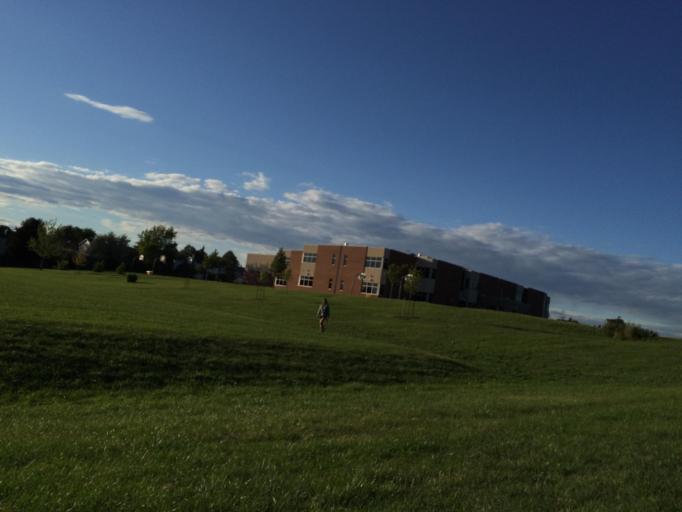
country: CA
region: Ontario
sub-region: Wellington County
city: Guelph
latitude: 43.5233
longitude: -80.2815
